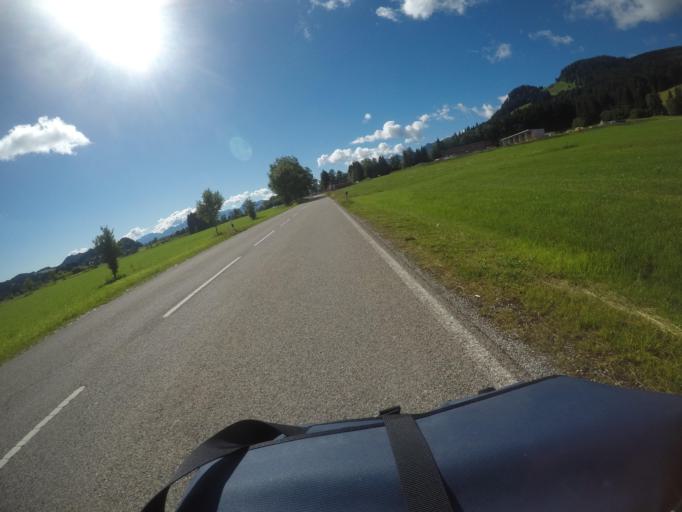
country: DE
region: Bavaria
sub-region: Swabia
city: Nesselwang
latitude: 47.6091
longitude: 10.5300
